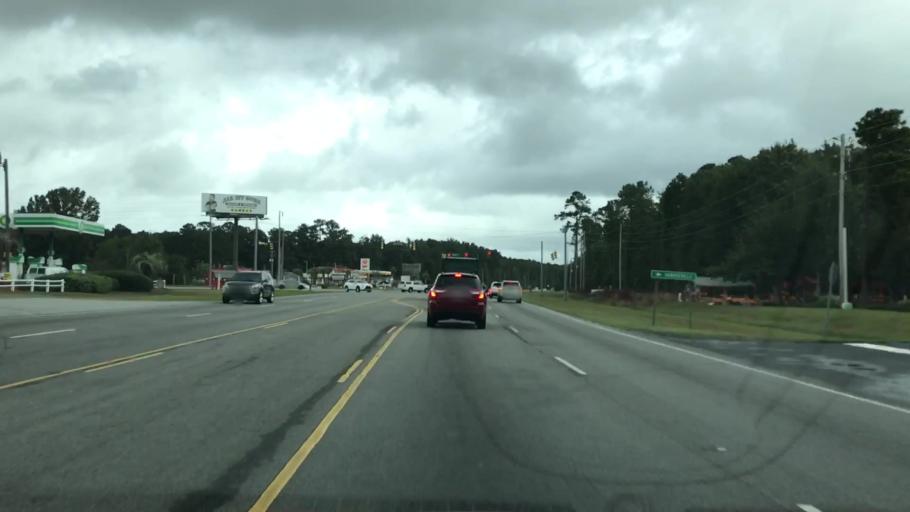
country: US
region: South Carolina
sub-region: Beaufort County
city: Bluffton
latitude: 32.3389
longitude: -80.9284
